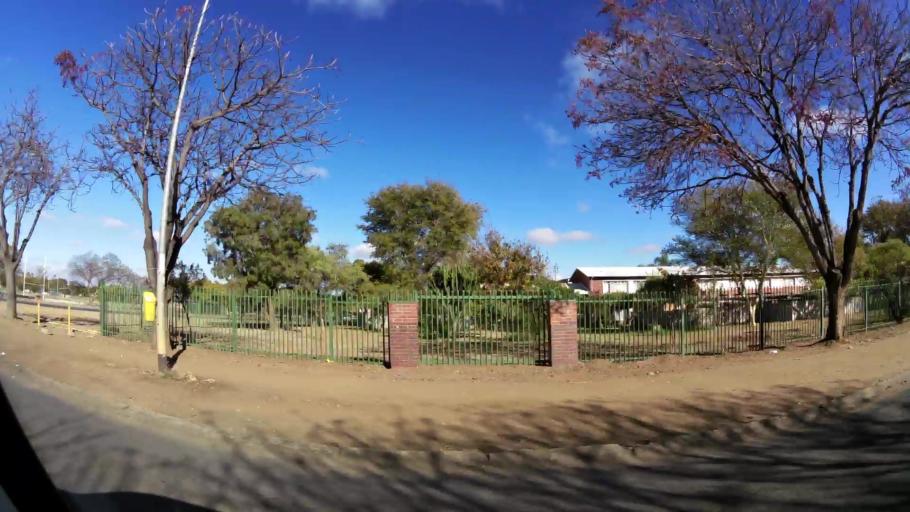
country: ZA
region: Limpopo
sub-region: Capricorn District Municipality
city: Polokwane
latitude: -23.8966
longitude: 29.4569
